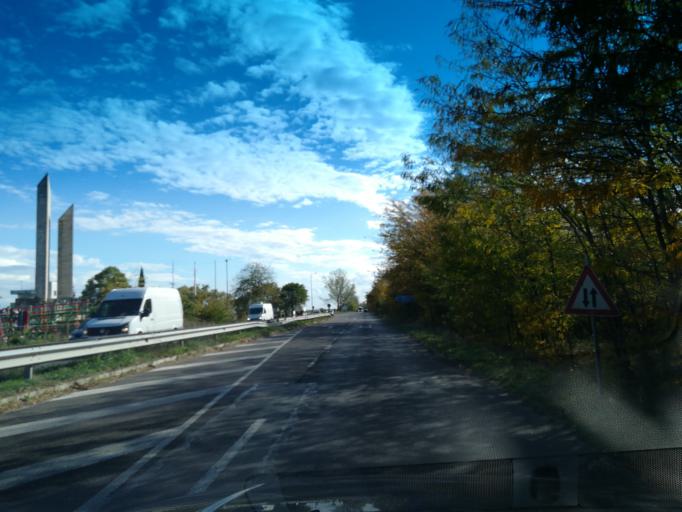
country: BG
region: Stara Zagora
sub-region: Obshtina Stara Zagora
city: Stara Zagora
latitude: 42.3866
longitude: 25.6484
